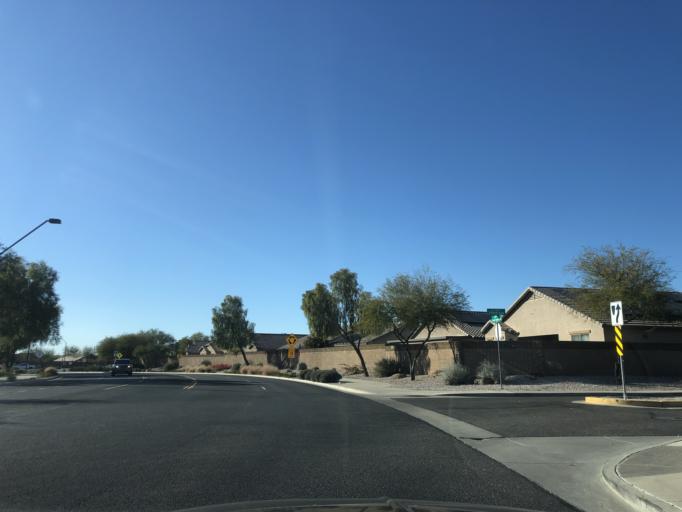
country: US
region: Arizona
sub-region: Maricopa County
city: Buckeye
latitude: 33.4207
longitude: -112.6016
